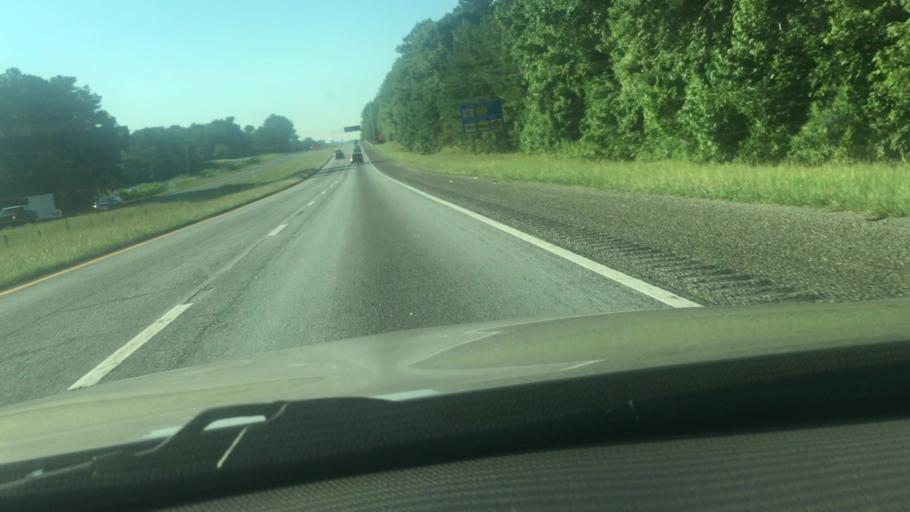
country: US
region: South Carolina
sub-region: Lexington County
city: Irmo
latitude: 34.1127
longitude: -81.1892
